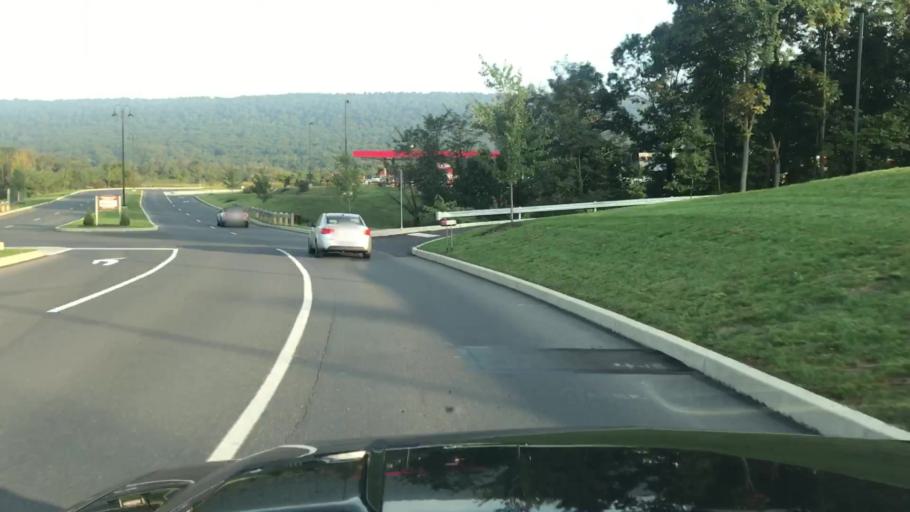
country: US
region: Pennsylvania
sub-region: Cumberland County
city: Enola
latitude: 40.2903
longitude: -76.9751
